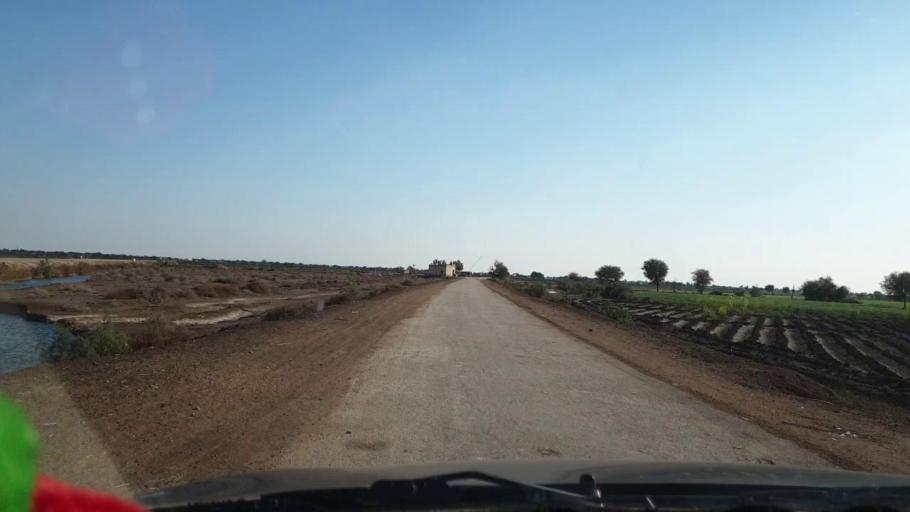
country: PK
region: Sindh
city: Sinjhoro
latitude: 26.0075
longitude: 68.8381
